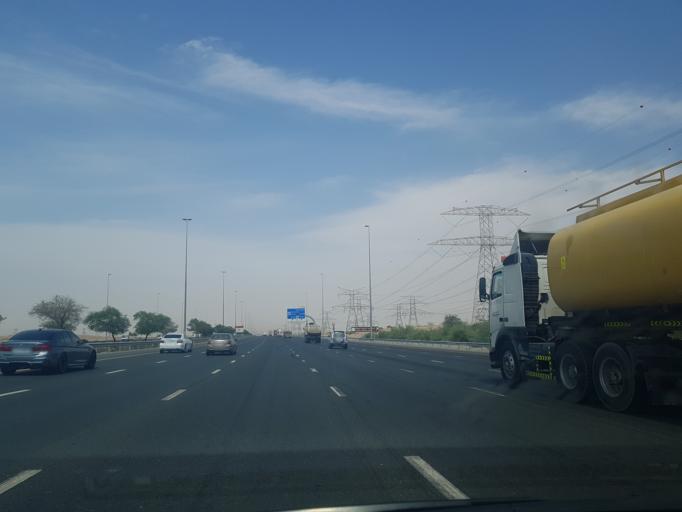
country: AE
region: Ash Shariqah
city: Sharjah
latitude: 25.2174
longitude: 55.5566
